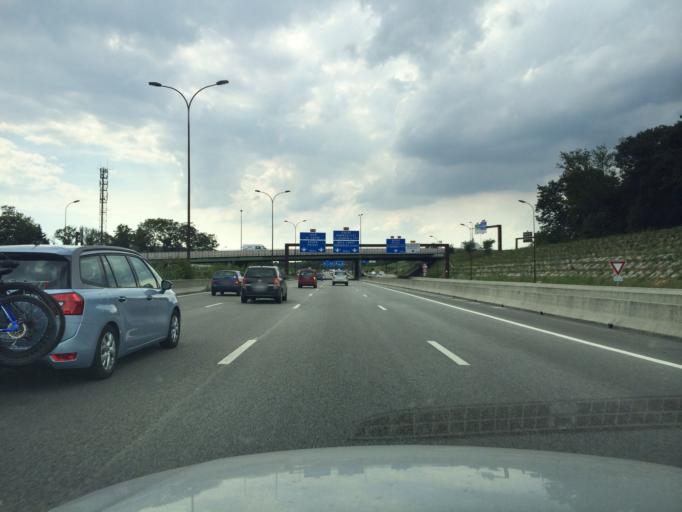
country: FR
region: Ile-de-France
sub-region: Departement des Yvelines
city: Rocquencourt
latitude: 48.8405
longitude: 2.1130
